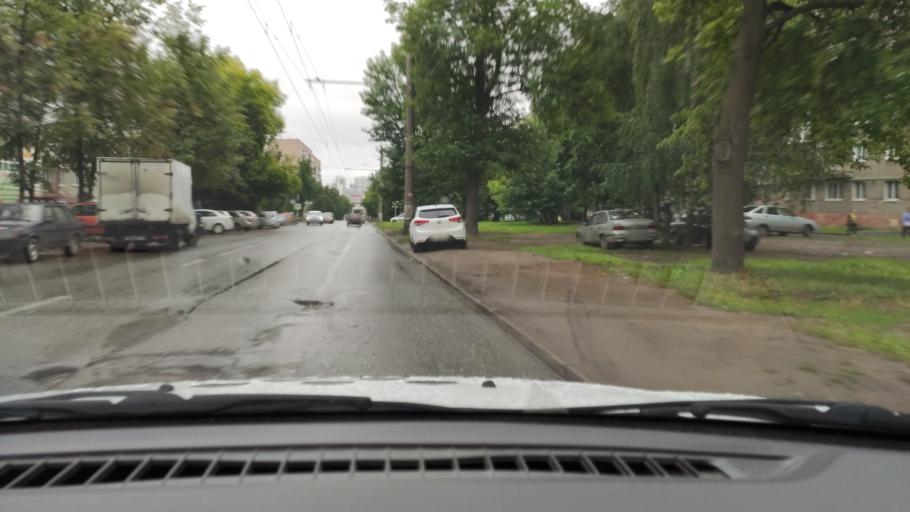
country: RU
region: Udmurtiya
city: Izhevsk
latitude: 56.8765
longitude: 53.1874
